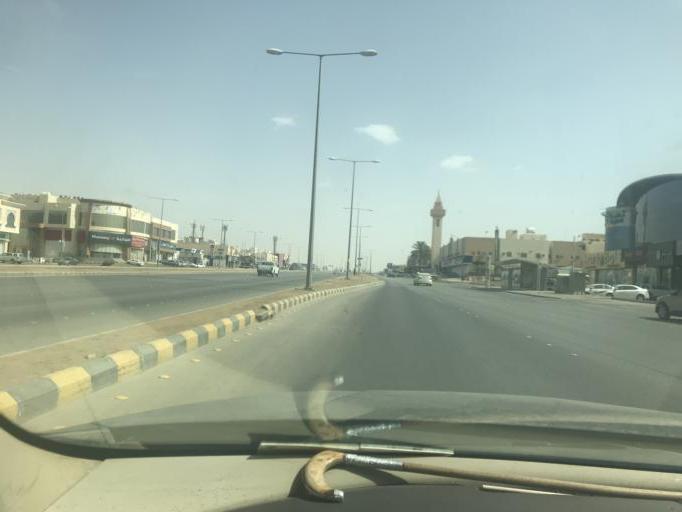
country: SA
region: Ar Riyad
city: Riyadh
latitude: 24.7729
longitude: 46.7102
